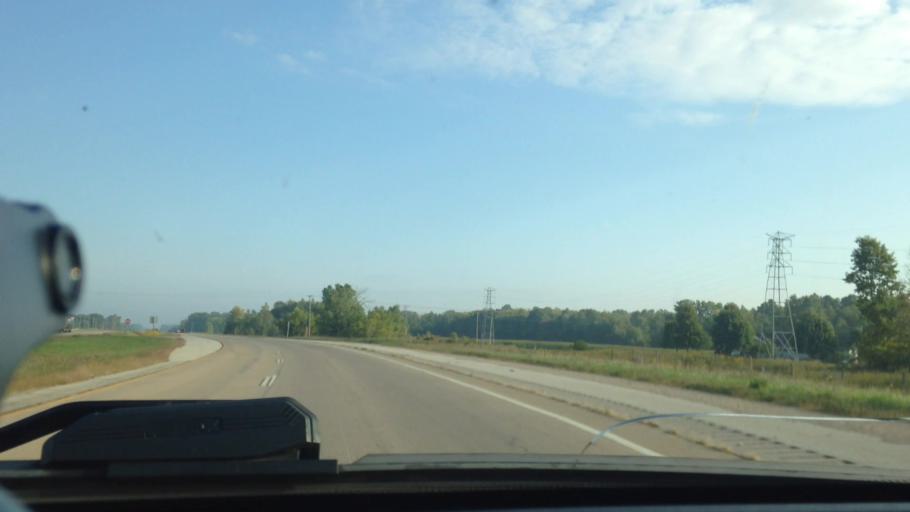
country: US
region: Wisconsin
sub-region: Oconto County
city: Oconto Falls
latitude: 44.9922
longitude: -88.0453
